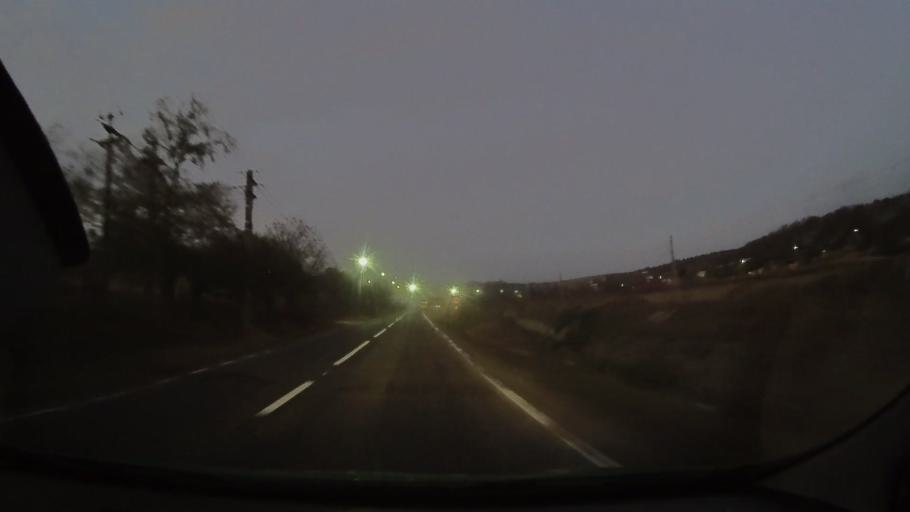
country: RO
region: Constanta
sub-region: Comuna Ion Corvin
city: Ion Corvin
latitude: 44.1082
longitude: 27.8019
